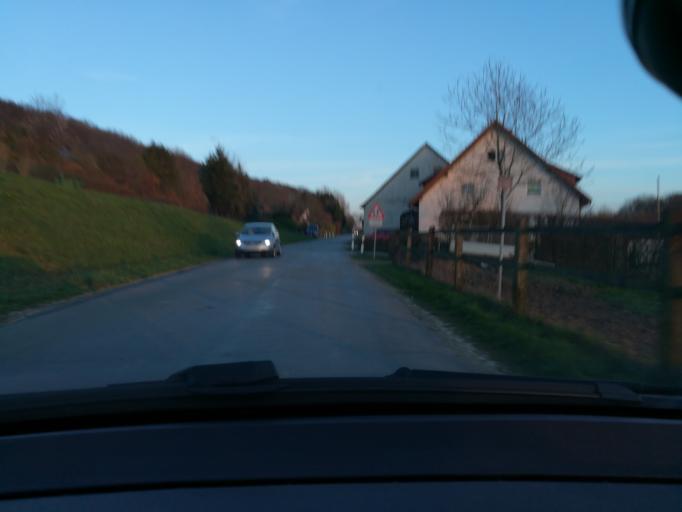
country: DE
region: North Rhine-Westphalia
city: Halle
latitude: 52.0878
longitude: 8.3570
